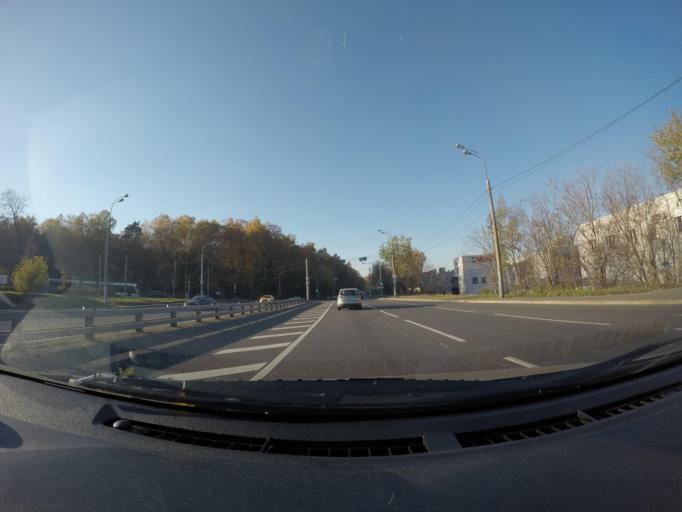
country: RU
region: Moscow
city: Sokol'niki
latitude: 55.8135
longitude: 37.6880
